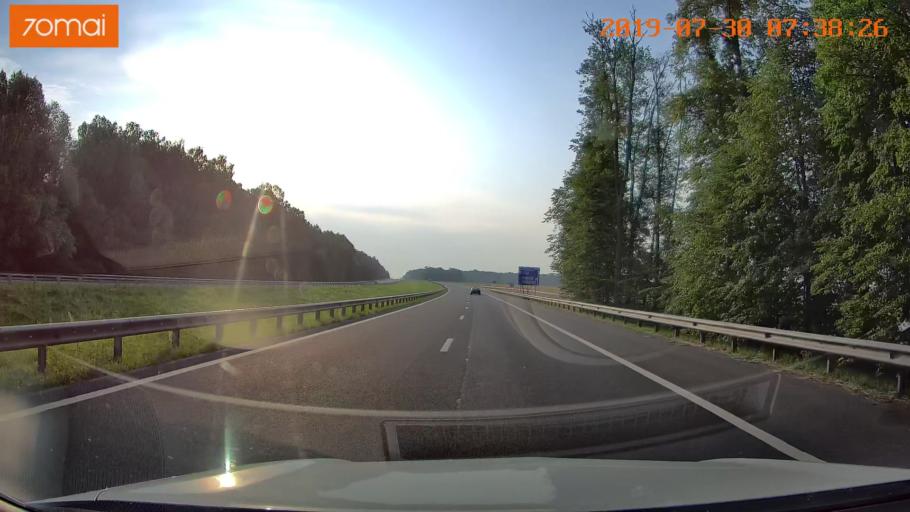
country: RU
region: Kaliningrad
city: Gvardeysk
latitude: 54.6501
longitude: 21.1684
